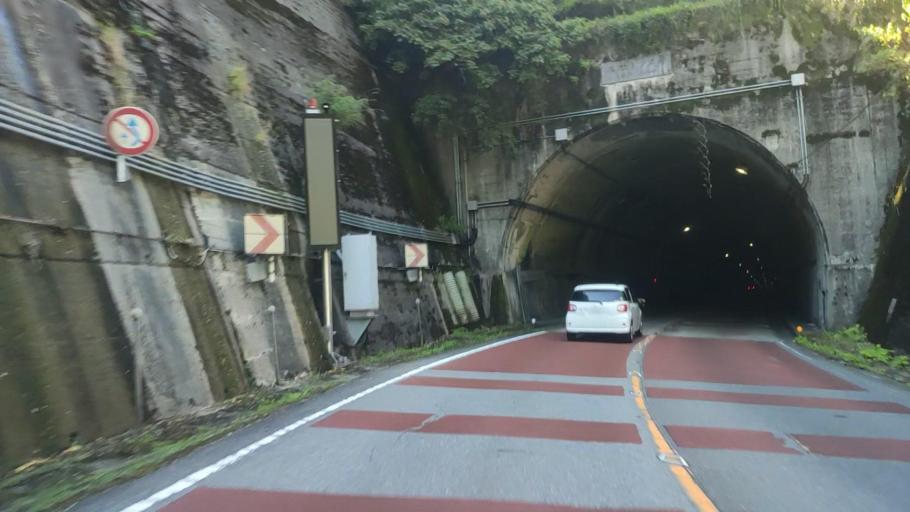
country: JP
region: Nara
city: Yoshino-cho
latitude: 34.3614
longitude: 135.9173
